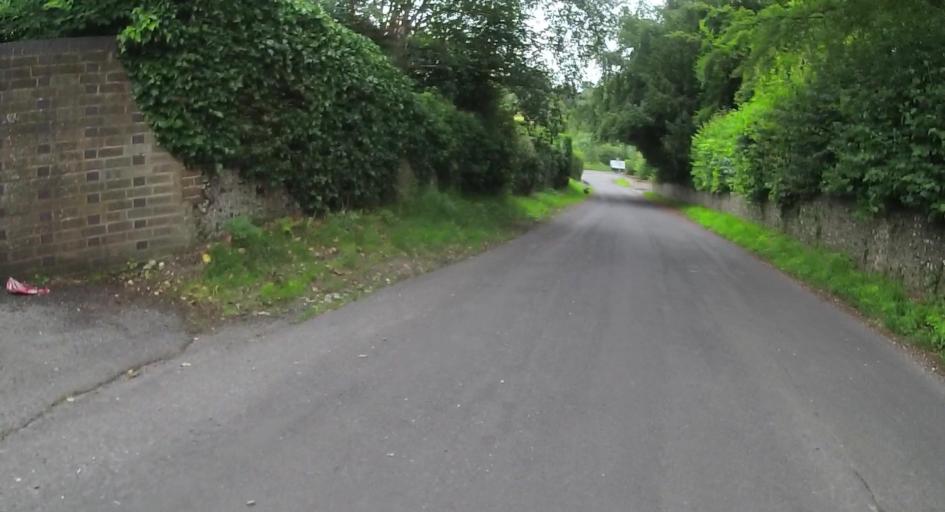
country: GB
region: England
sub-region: Hampshire
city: Kings Worthy
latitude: 51.0946
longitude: -1.2273
